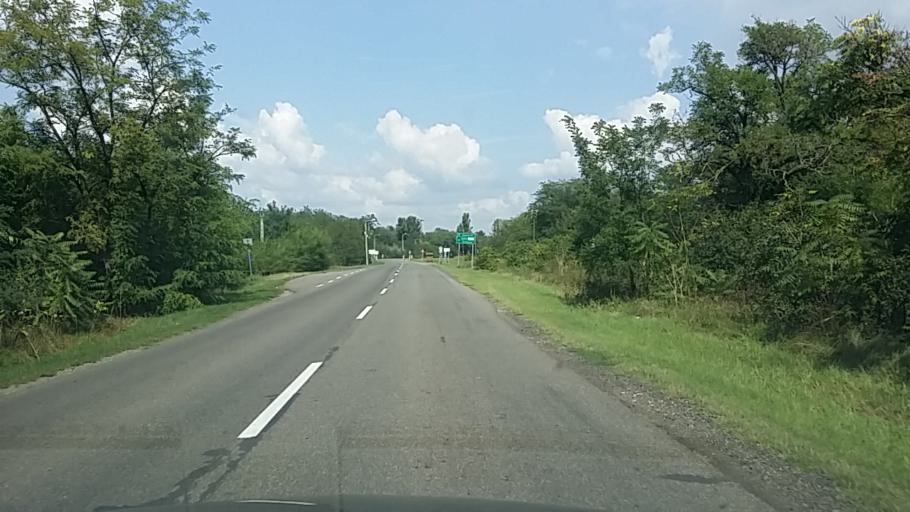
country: HU
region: Bacs-Kiskun
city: Lakitelek
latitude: 46.8569
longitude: 19.9819
